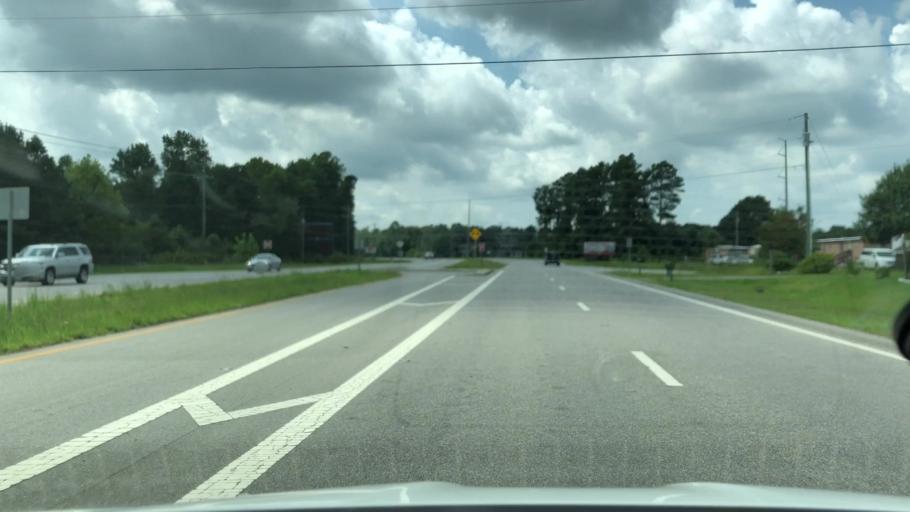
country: US
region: North Carolina
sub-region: Beaufort County
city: Washington
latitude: 35.4778
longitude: -77.1164
